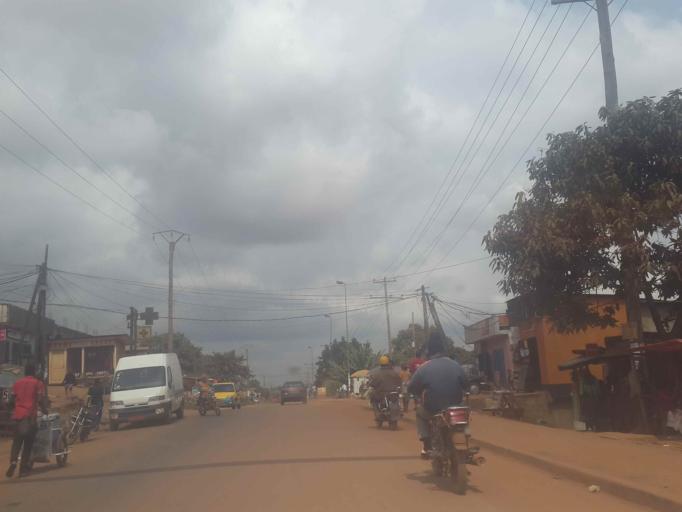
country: CM
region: Centre
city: Yaounde
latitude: 3.8751
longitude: 11.4749
